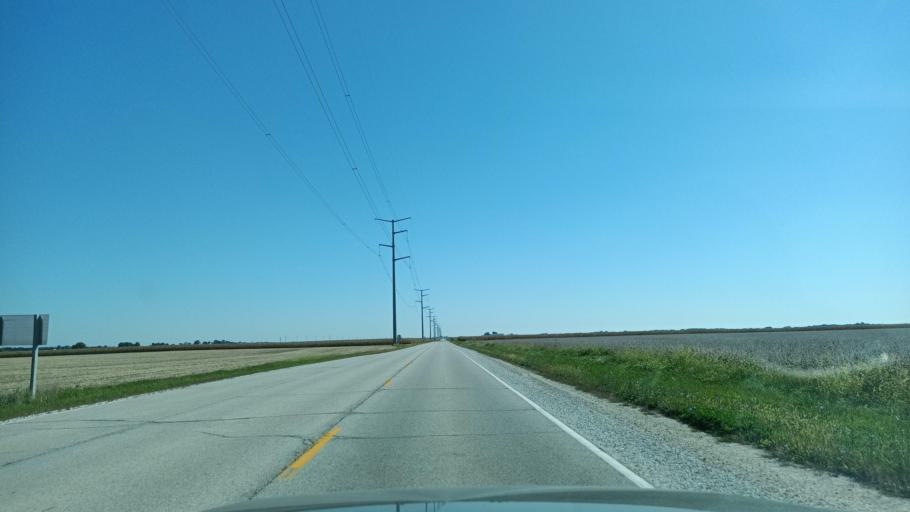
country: US
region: Illinois
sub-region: Peoria County
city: Elmwood
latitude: 40.9024
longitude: -90.0134
